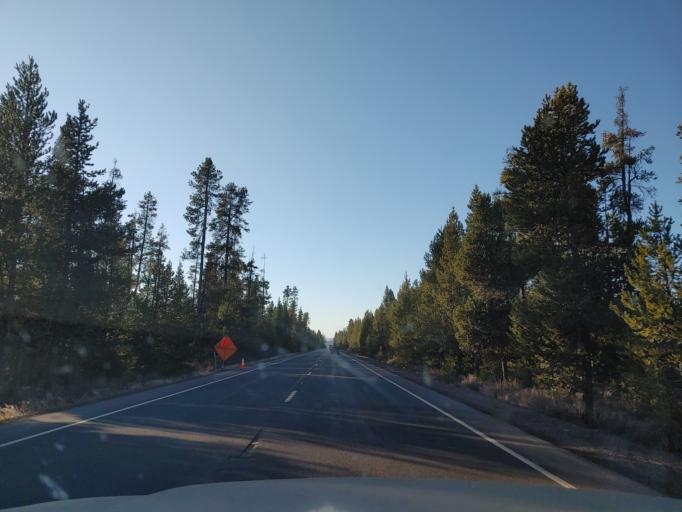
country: US
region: Oregon
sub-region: Deschutes County
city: La Pine
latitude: 43.3854
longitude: -121.8061
